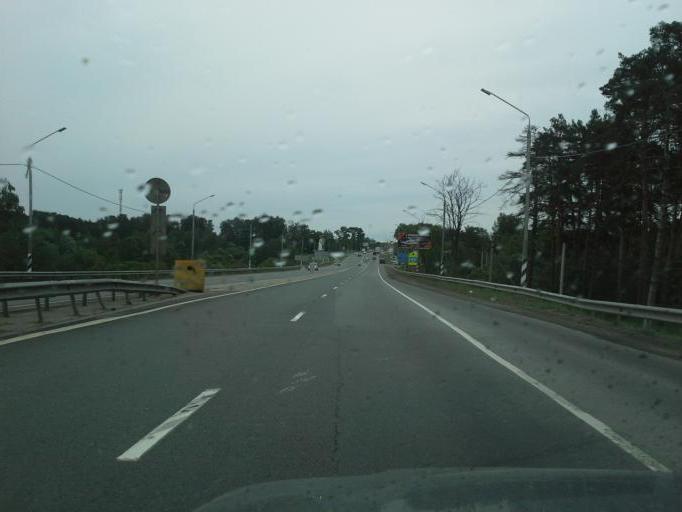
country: RU
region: Moskovskaya
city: Malaya Dubna
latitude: 55.8991
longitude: 39.0568
